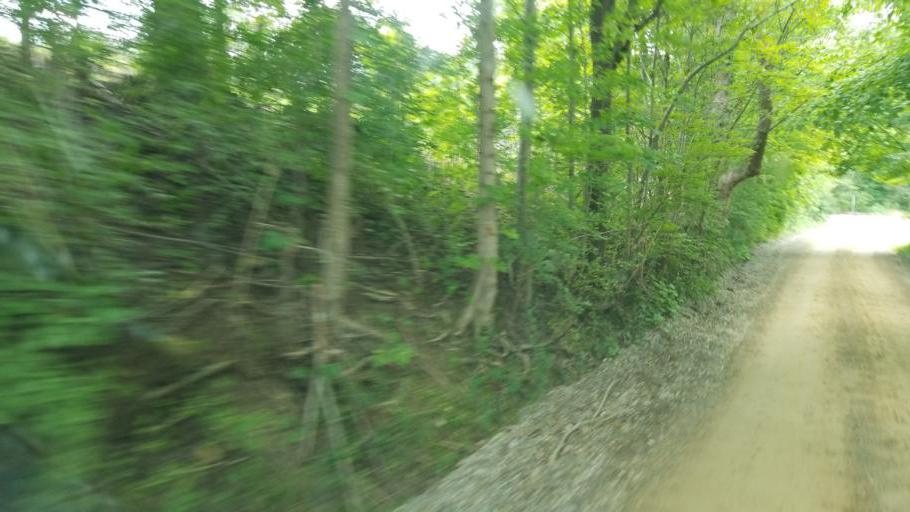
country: US
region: Ohio
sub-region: Knox County
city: Mount Vernon
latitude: 40.3788
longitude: -82.5581
